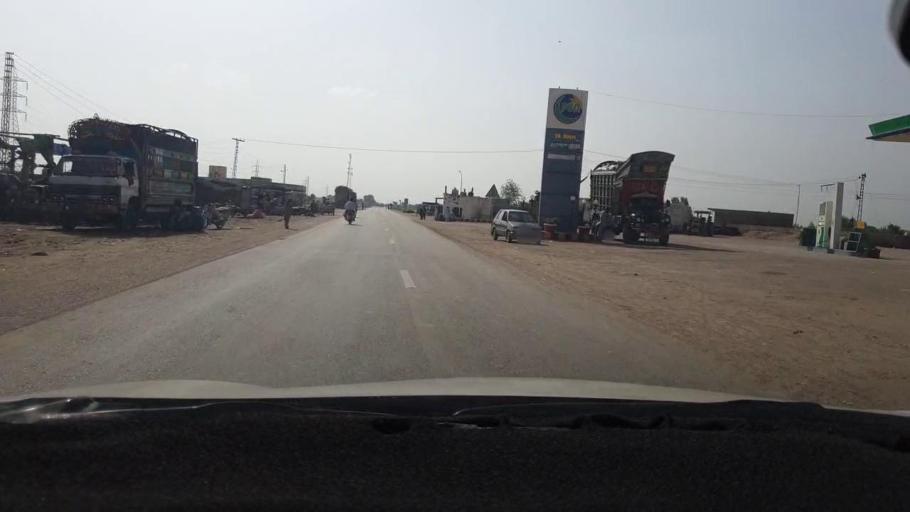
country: PK
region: Sindh
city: Jhol
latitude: 25.8810
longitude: 69.0391
